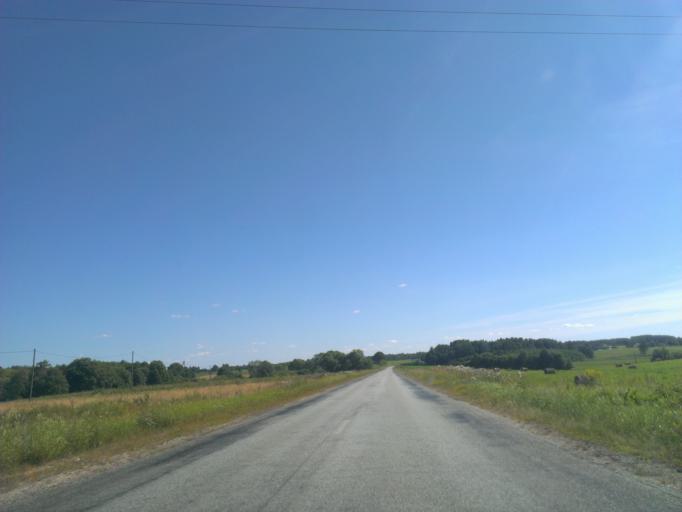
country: LV
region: Malpils
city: Malpils
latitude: 57.0189
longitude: 24.8542
